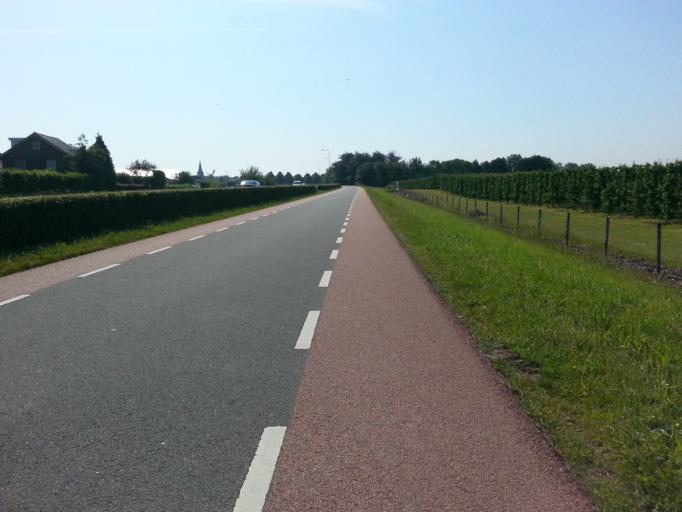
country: NL
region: Utrecht
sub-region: Gemeente Wijk bij Duurstede
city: Wijk bij Duurstede
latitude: 52.0020
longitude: 5.2983
